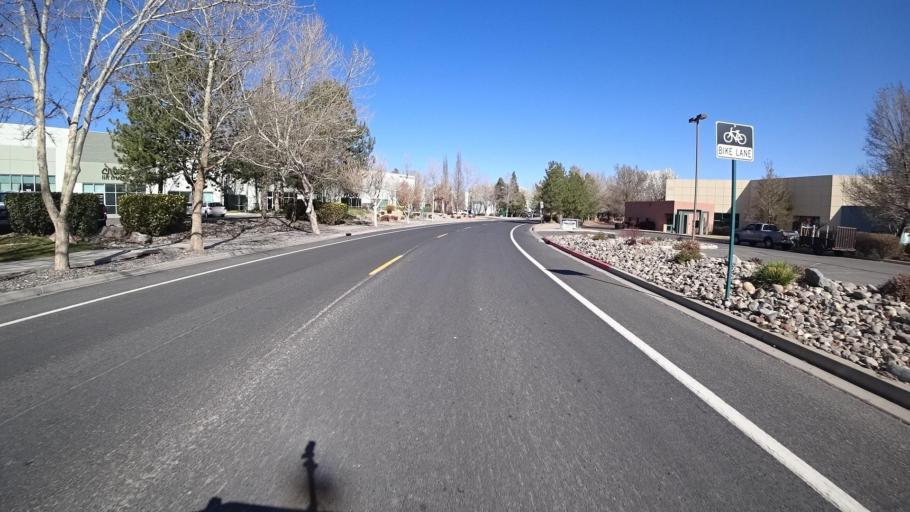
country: US
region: Nevada
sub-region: Washoe County
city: Sparks
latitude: 39.4597
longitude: -119.7762
